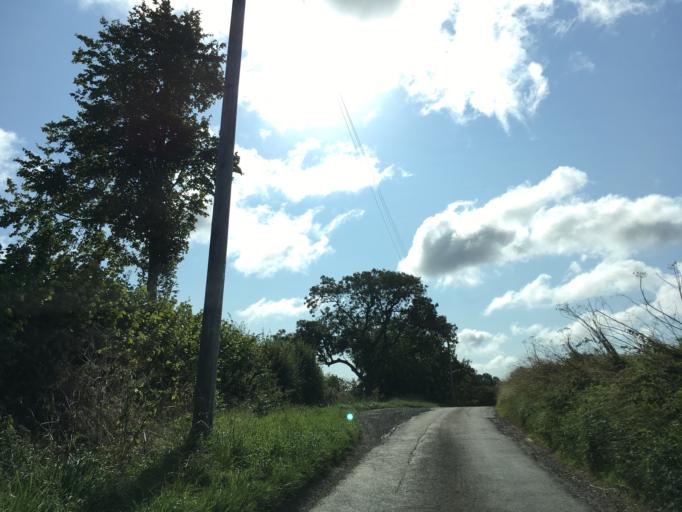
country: GB
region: England
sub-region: South Gloucestershire
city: Hinton
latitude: 51.5098
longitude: -2.3609
